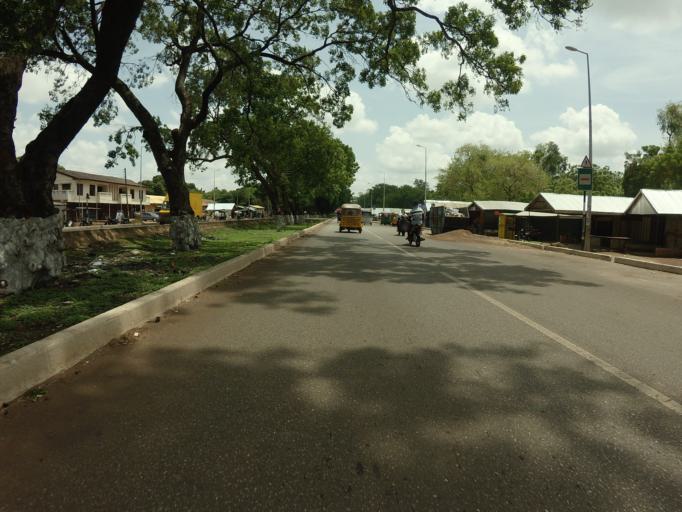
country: GH
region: Northern
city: Tamale
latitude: 9.4044
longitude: -0.8547
